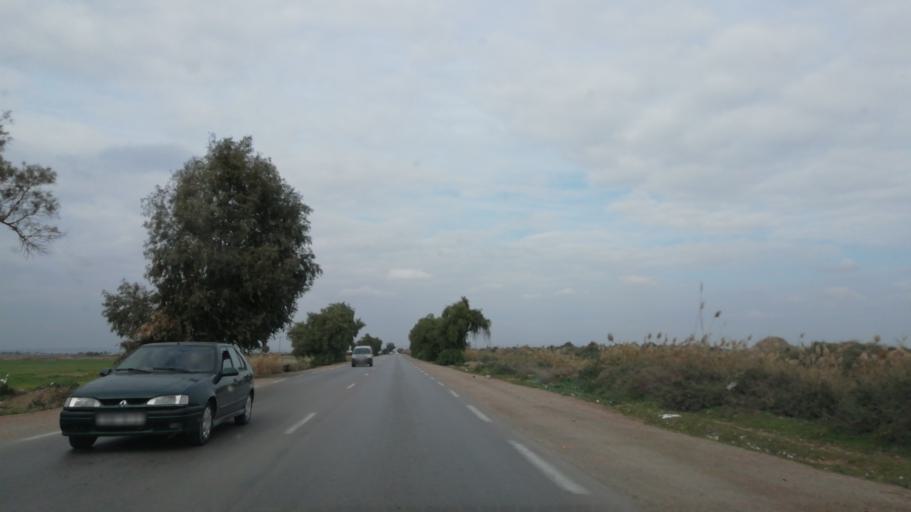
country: DZ
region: Mascara
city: Mascara
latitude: 35.6384
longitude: 0.0606
